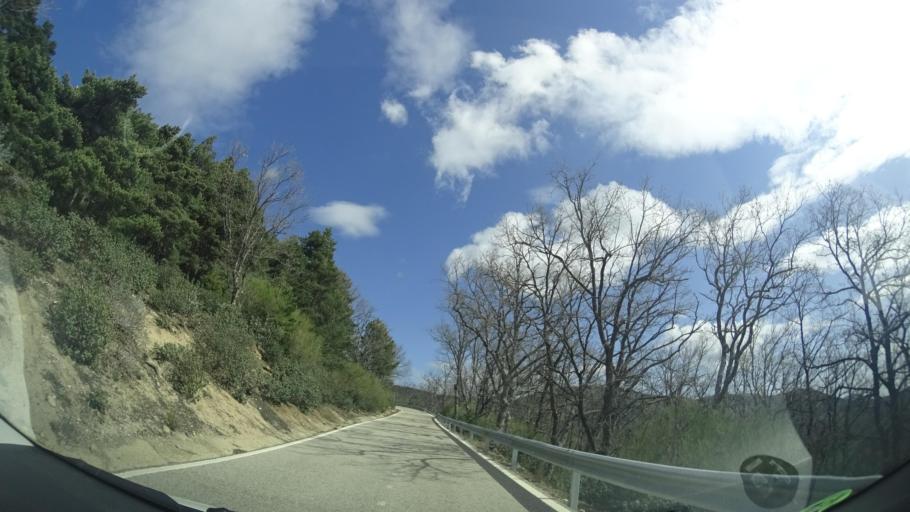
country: ES
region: Madrid
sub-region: Provincia de Madrid
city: Miraflores de la Sierra
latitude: 40.8491
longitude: -3.7659
